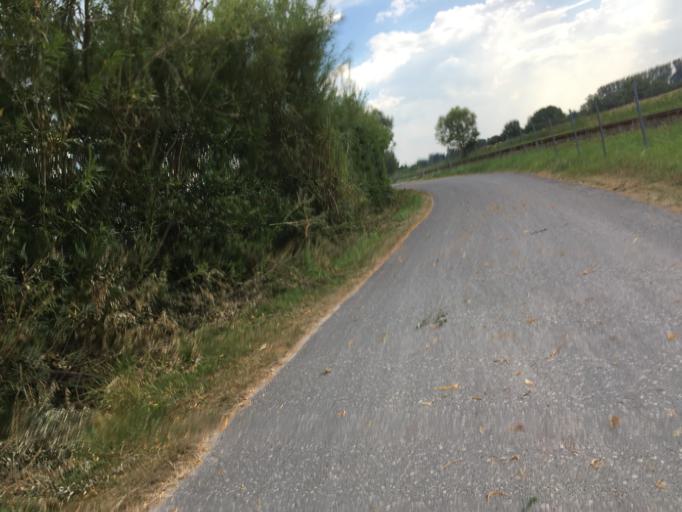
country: DE
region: Brandenburg
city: Zehdenick
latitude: 52.9930
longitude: 13.3207
